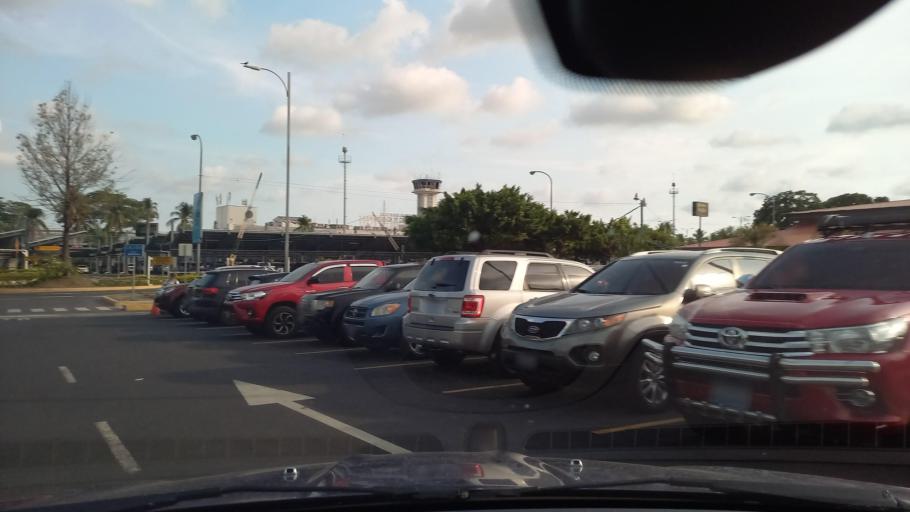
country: SV
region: La Paz
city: El Rosario
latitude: 13.4471
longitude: -89.0566
